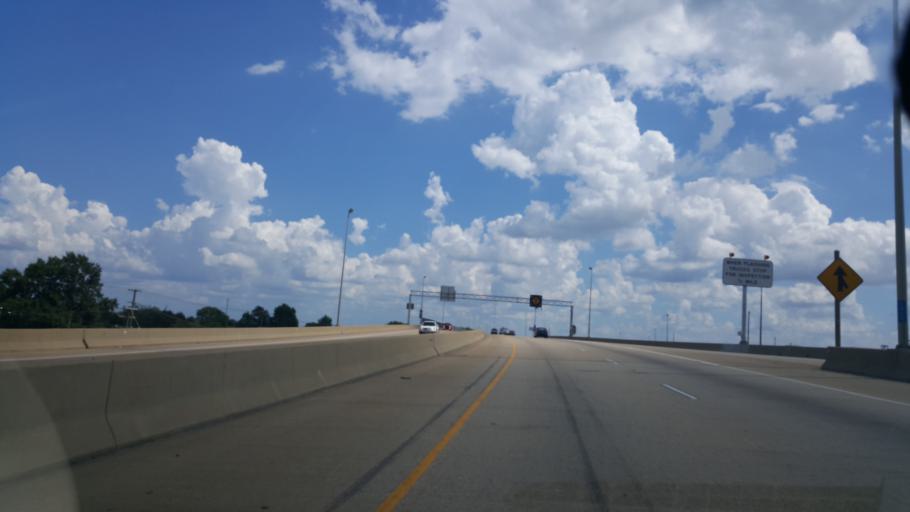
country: US
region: Virginia
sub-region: City of Newport News
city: Newport News
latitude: 36.9763
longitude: -76.4220
